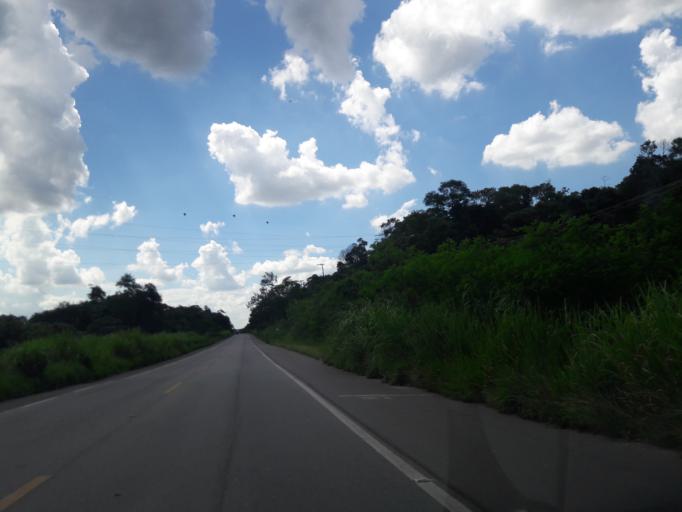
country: BR
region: Sao Paulo
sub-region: Campo Limpo Paulista
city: Campo Limpo Paulista
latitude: -23.2210
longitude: -46.7889
